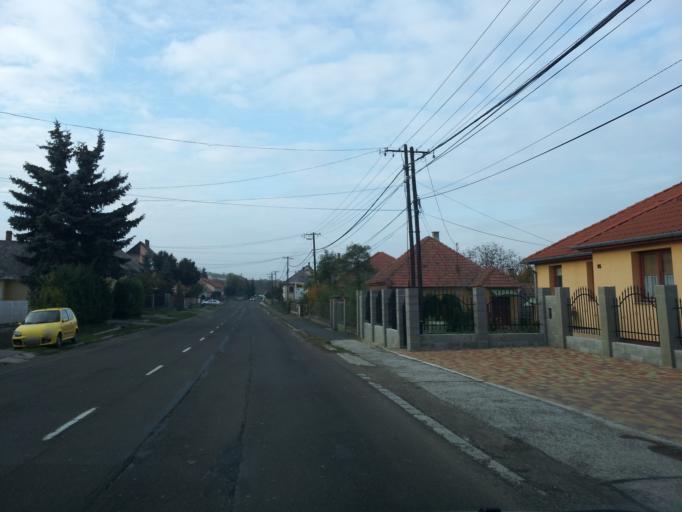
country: HU
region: Gyor-Moson-Sopron
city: Pannonhalma
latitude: 47.5188
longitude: 17.7522
